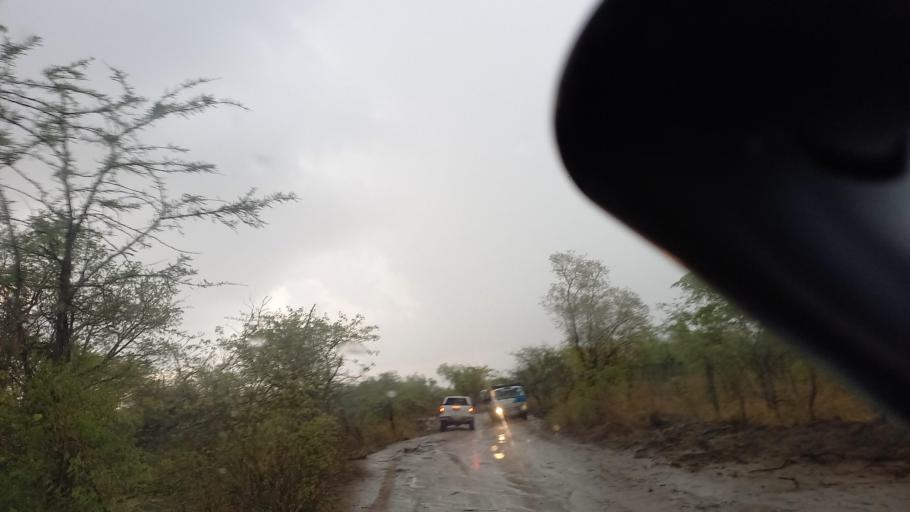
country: ZM
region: Lusaka
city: Kafue
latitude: -15.9430
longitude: 28.2171
